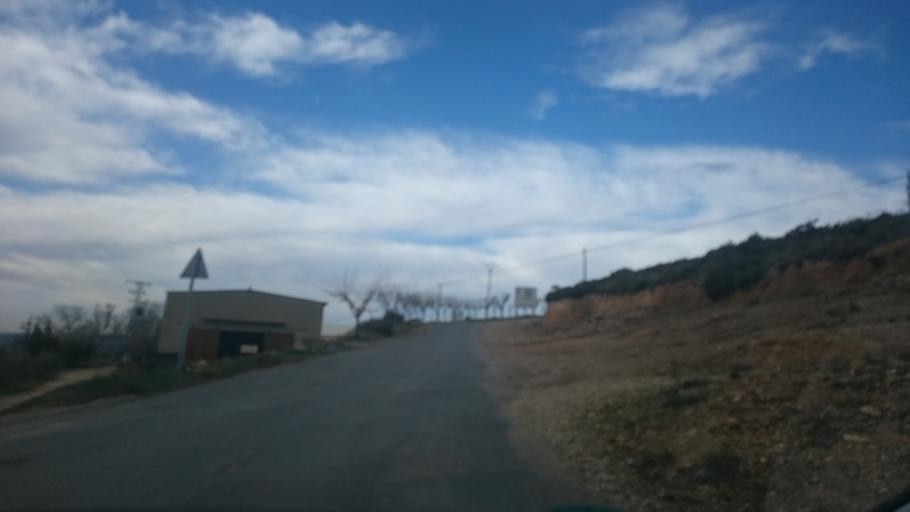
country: ES
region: Aragon
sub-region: Provincia de Huesca
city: Alquezar
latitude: 42.1670
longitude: 0.0191
